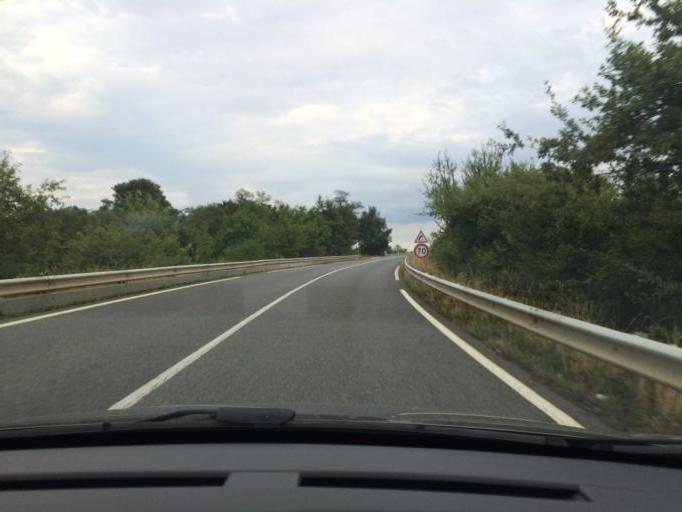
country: FR
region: Rhone-Alpes
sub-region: Departement du Rhone
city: Saint-Laurent-de-Mure
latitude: 45.6998
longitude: 5.0684
